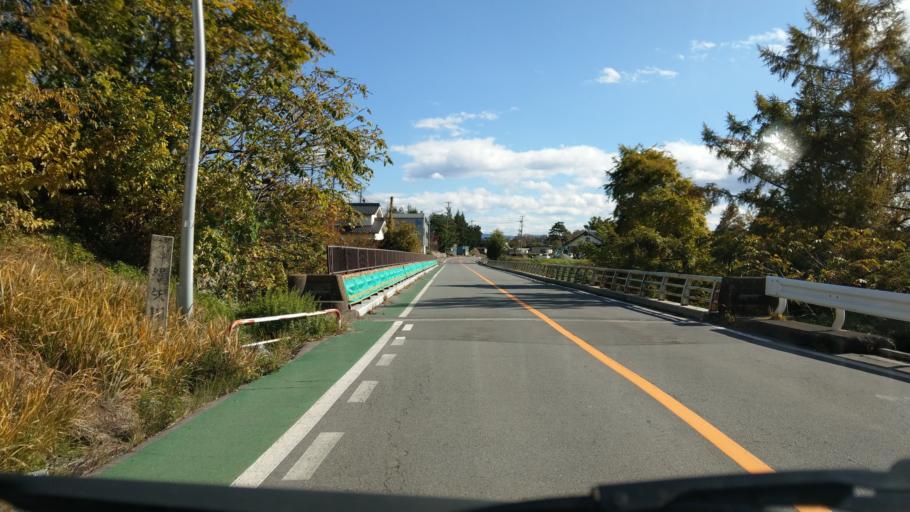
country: JP
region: Nagano
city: Komoro
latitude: 36.3078
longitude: 138.4286
